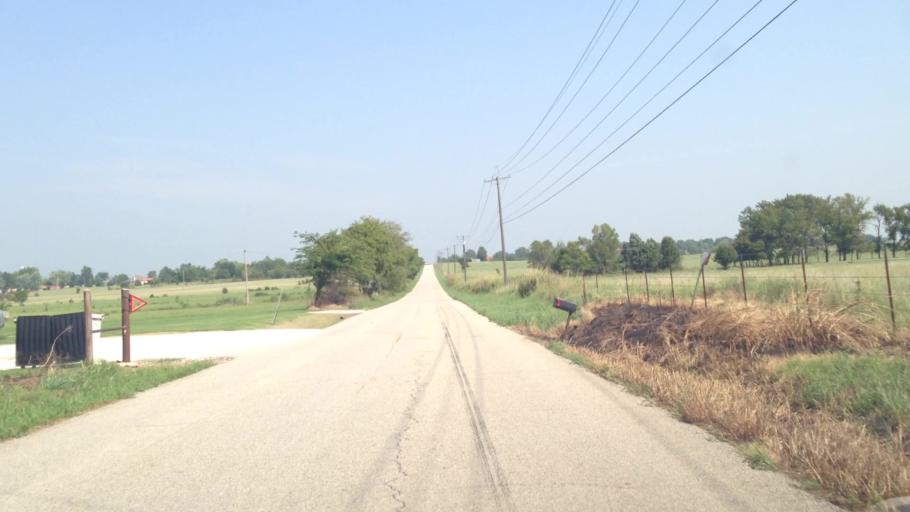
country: US
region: Oklahoma
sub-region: Craig County
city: Vinita
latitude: 36.6448
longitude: -95.1255
